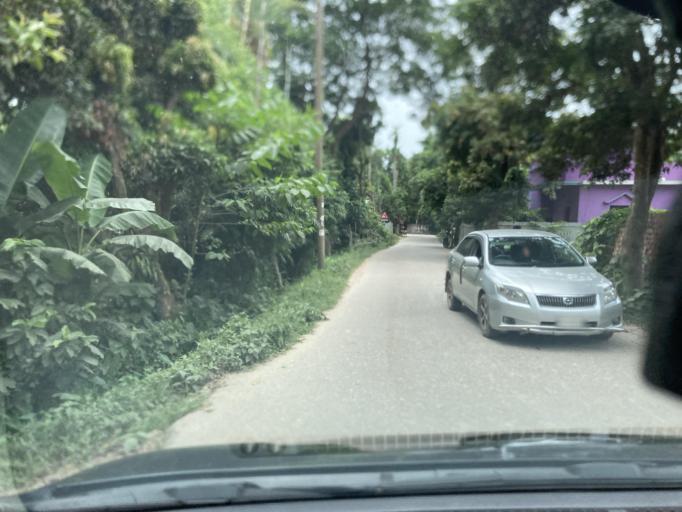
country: BD
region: Dhaka
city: Dohar
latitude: 23.8009
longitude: 90.0470
